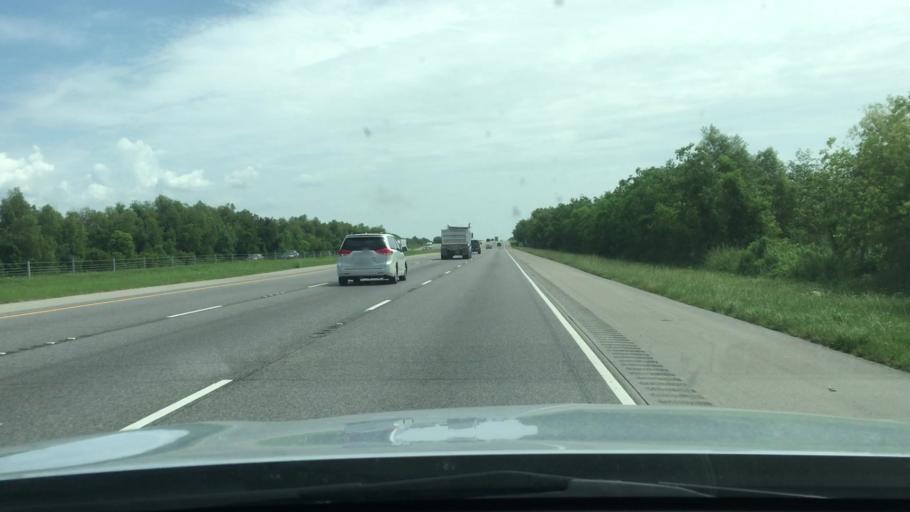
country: US
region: Louisiana
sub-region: Saint Tammany Parish
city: Eden Isle
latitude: 30.1279
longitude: -89.8769
